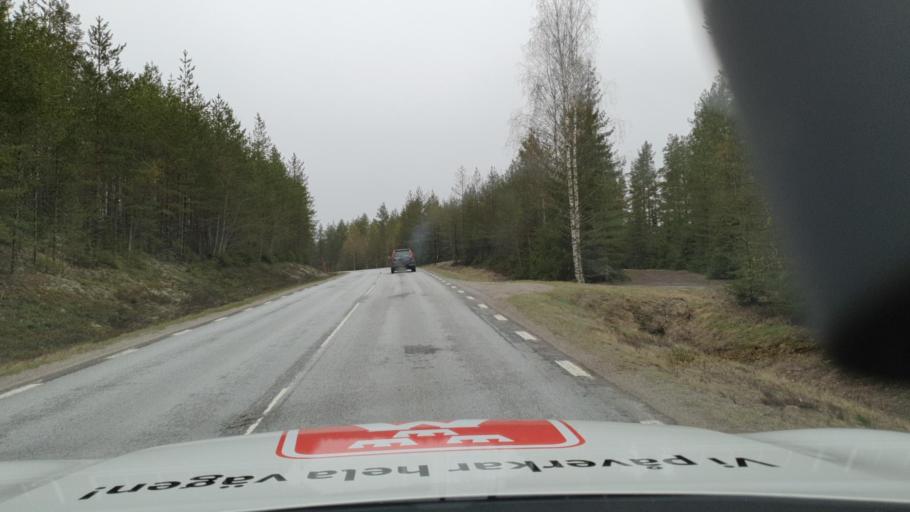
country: SE
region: Vaesterbotten
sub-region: Nordmalings Kommun
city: Nordmaling
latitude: 63.6102
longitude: 19.4195
